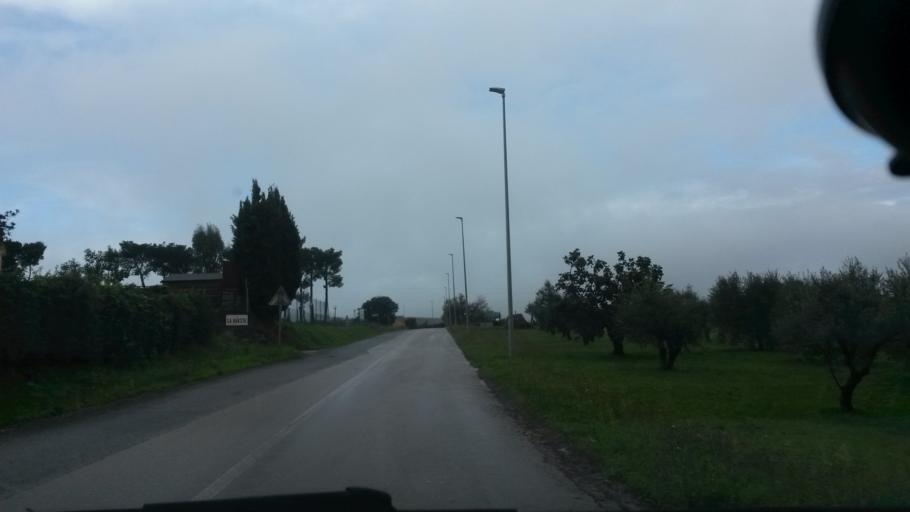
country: IT
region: Tuscany
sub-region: Provincia di Livorno
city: Rosignano Marittimo
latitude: 43.4154
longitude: 10.4635
